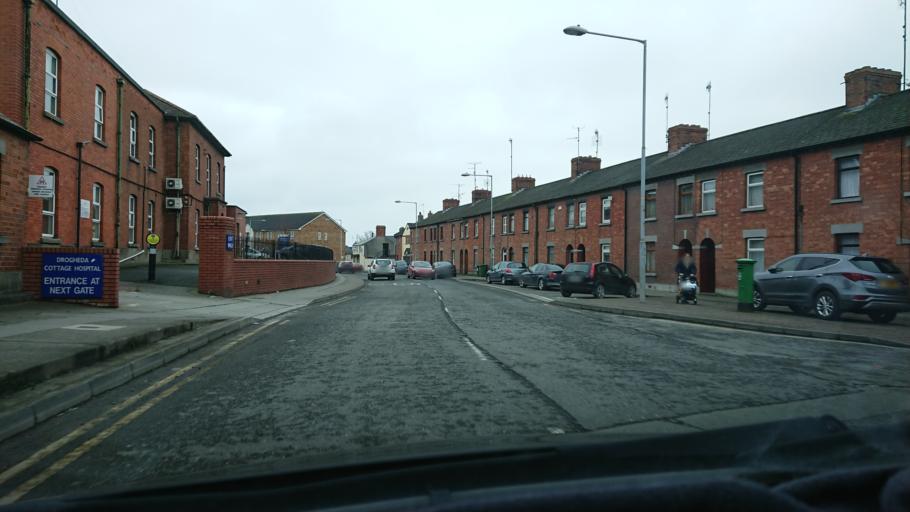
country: IE
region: Leinster
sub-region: Lu
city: Drogheda
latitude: 53.7190
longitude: -6.3444
